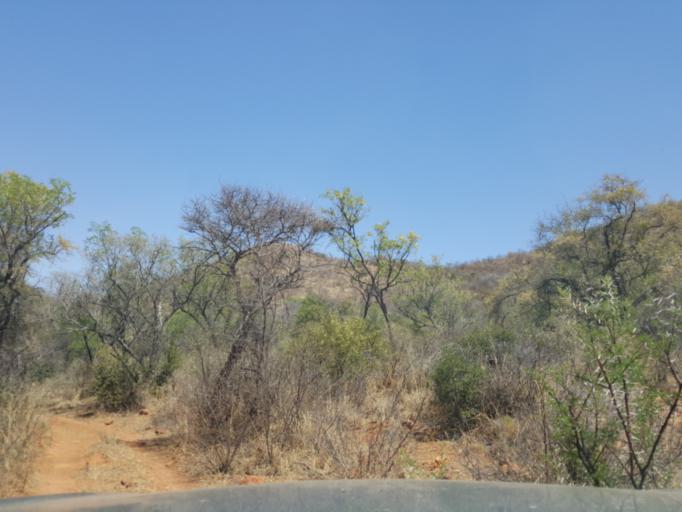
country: BW
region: South East
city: Lobatse
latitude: -25.1479
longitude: 25.6699
